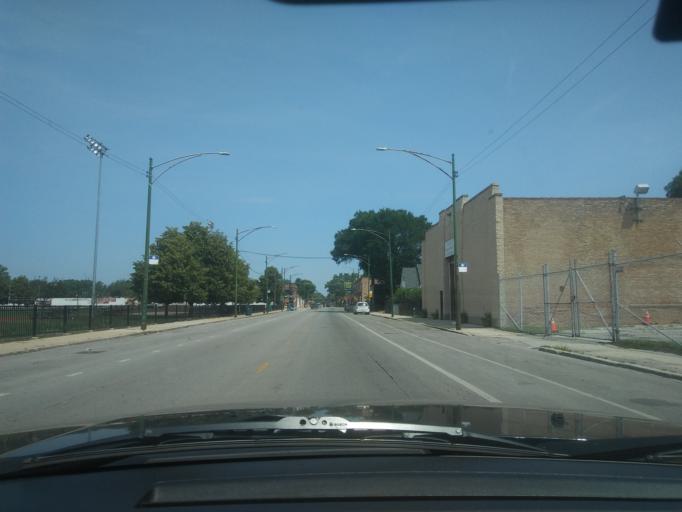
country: US
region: Illinois
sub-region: Cook County
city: Chicago
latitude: 41.7850
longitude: -87.6740
